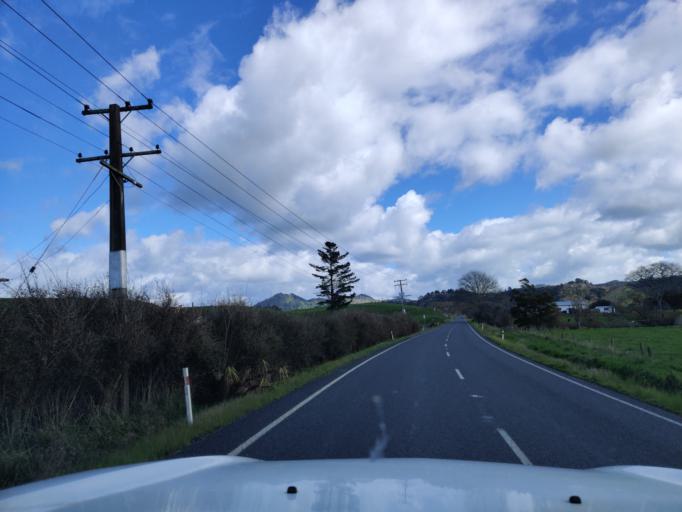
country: NZ
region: Waikato
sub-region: Waikato District
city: Ngaruawahia
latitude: -37.5784
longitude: 175.2272
